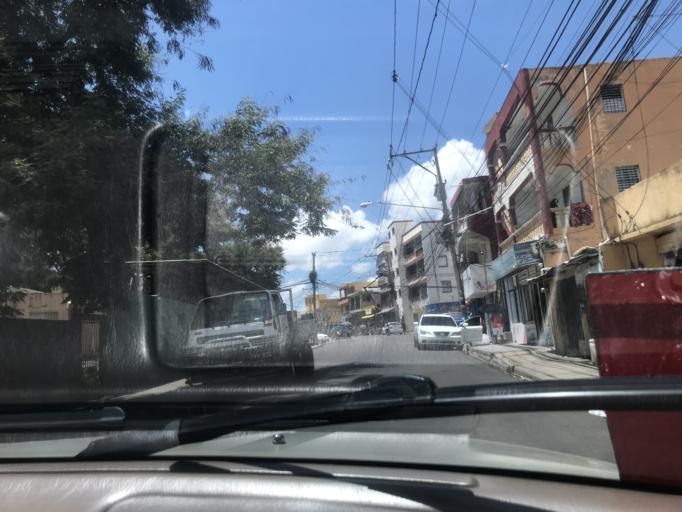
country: DO
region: Santiago
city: Santiago de los Caballeros
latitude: 19.4282
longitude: -70.6941
